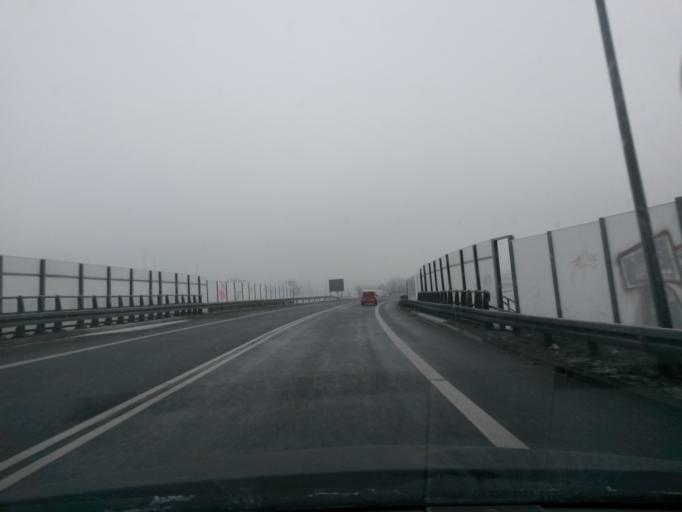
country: PL
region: Greater Poland Voivodeship
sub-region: Powiat gnieznienski
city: Gniezno
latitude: 52.5554
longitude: 17.6278
